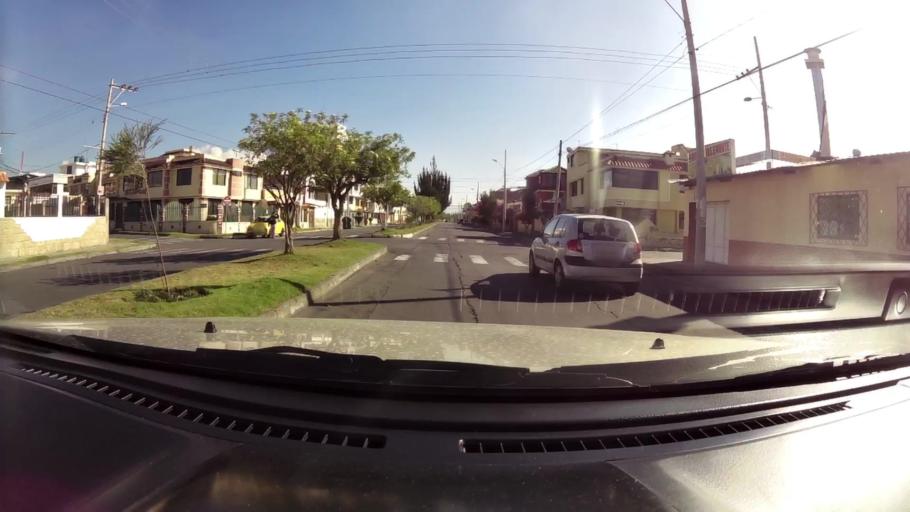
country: EC
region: Chimborazo
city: Riobamba
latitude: -1.6502
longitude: -78.6656
